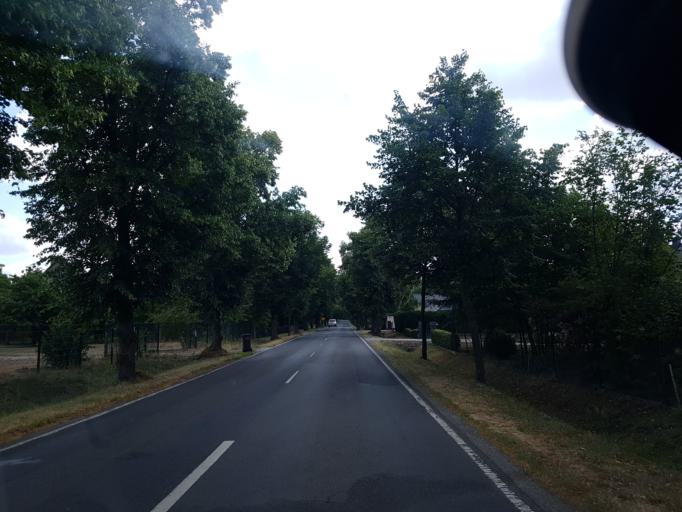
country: DE
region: Brandenburg
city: Drebkau
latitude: 51.6615
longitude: 14.2043
